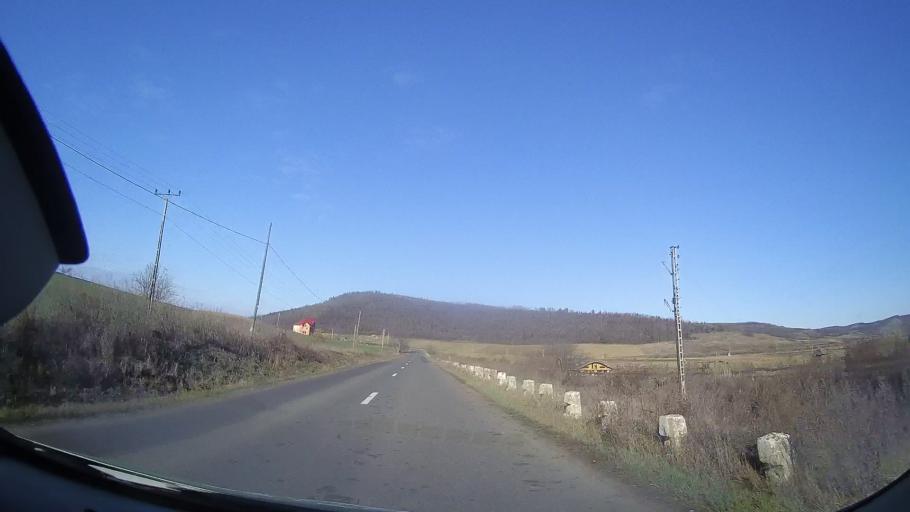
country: RO
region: Mures
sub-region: Comuna Mihesu de Campie
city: Mihesu de Campie
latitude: 46.6665
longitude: 24.1736
